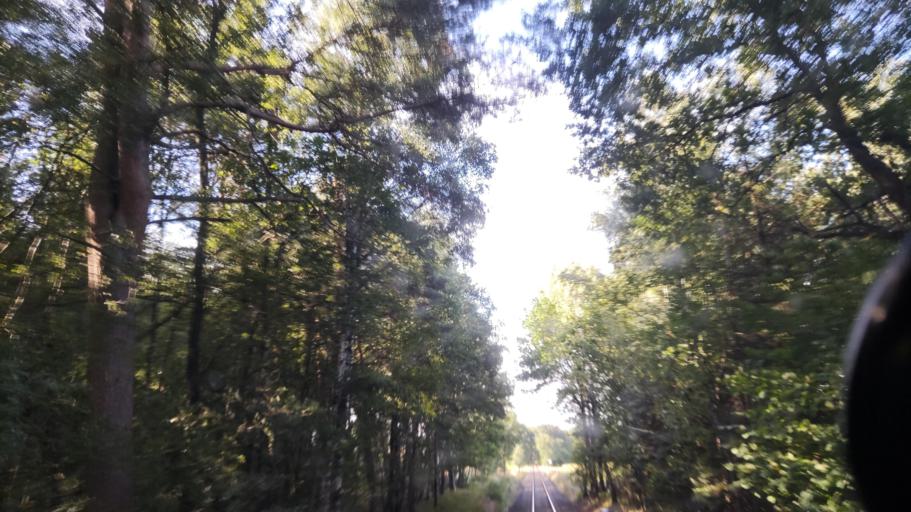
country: DE
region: Lower Saxony
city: Bispingen
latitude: 53.0391
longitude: 9.9374
